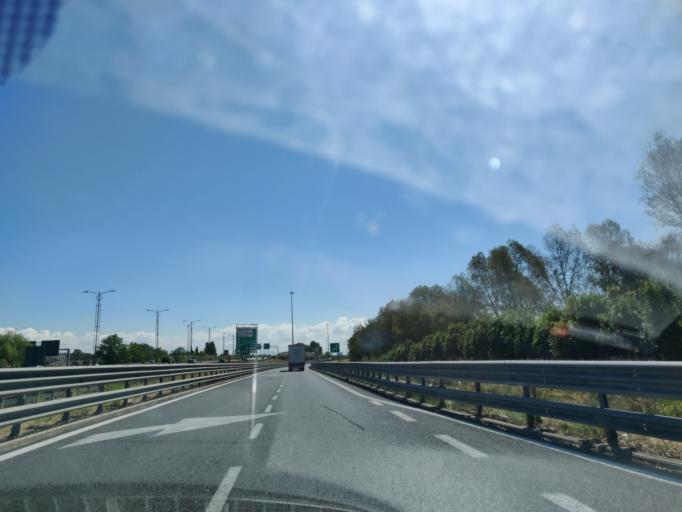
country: IT
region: Latium
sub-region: Citta metropolitana di Roma Capitale
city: Vitinia
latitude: 41.8175
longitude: 12.3842
